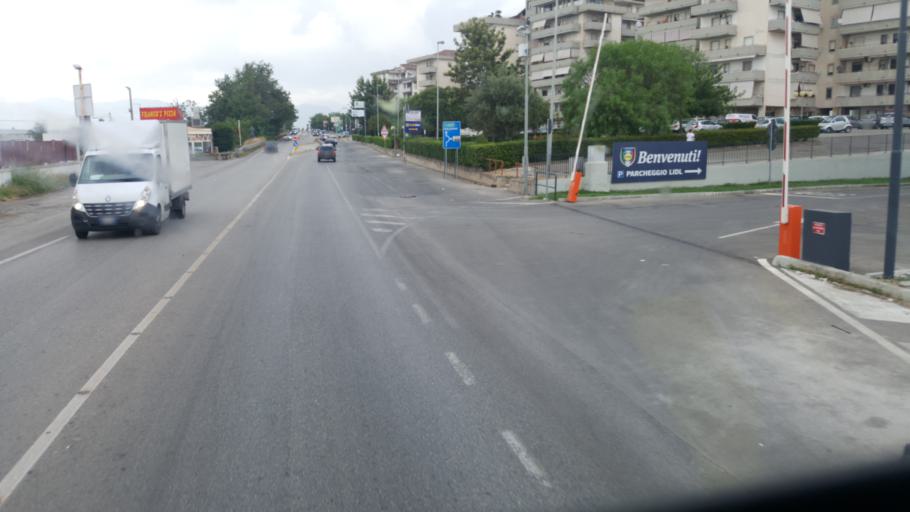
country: IT
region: Campania
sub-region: Provincia di Salerno
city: Battipaglia
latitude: 40.6042
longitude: 14.9735
